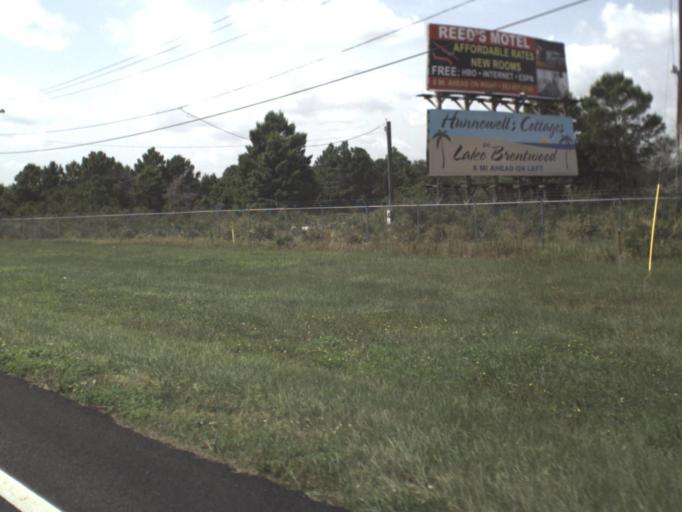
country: US
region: Florida
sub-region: Polk County
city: Frostproof
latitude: 27.7095
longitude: -81.5616
